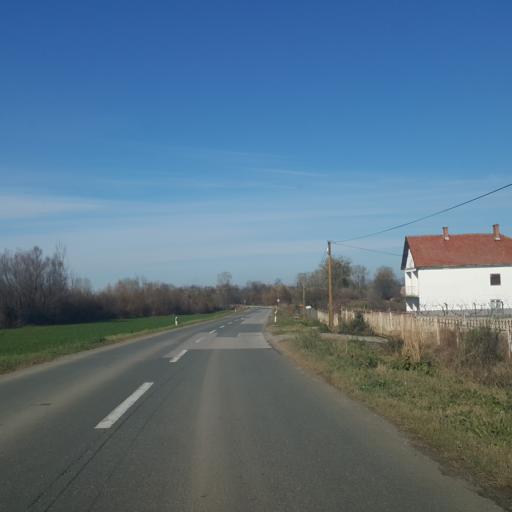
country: RS
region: Central Serbia
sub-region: Sumadijski Okrug
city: Raca
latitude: 44.2435
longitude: 20.8311
